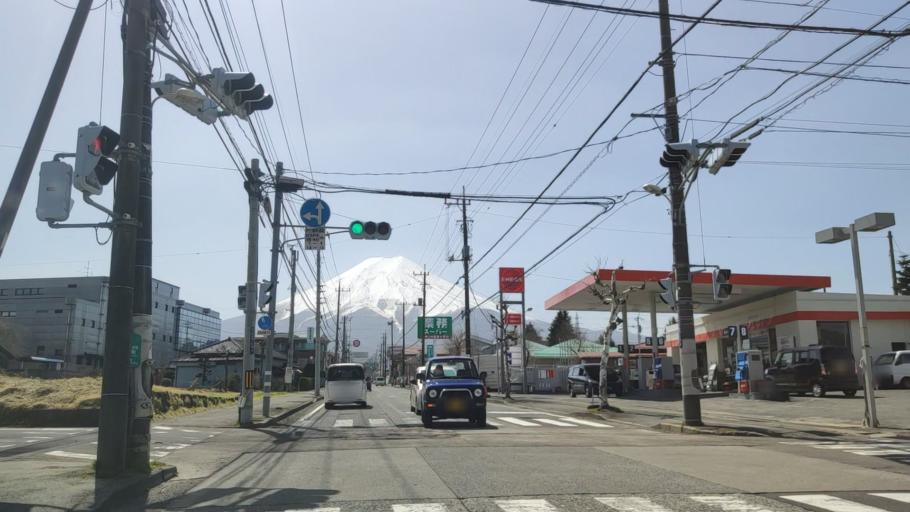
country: JP
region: Yamanashi
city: Fujikawaguchiko
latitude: 35.4761
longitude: 138.8006
